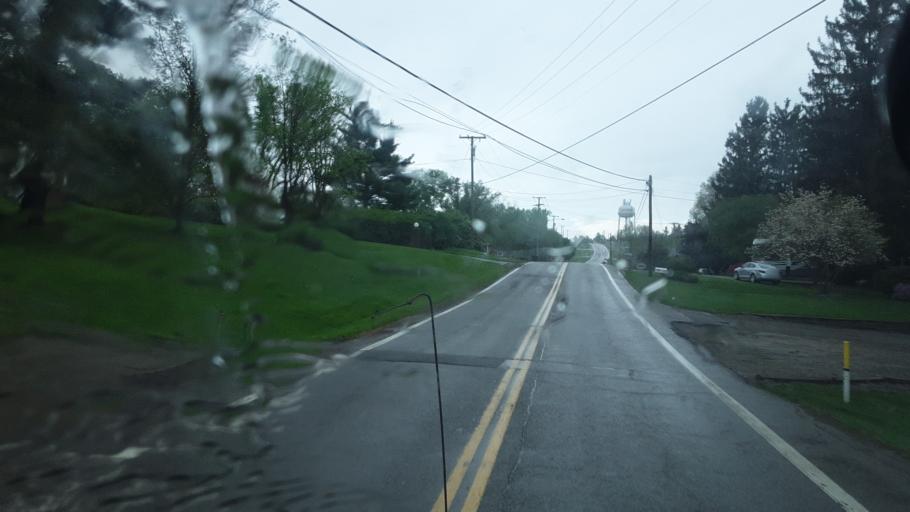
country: US
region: Ohio
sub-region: Muskingum County
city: New Concord
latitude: 40.0019
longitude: -81.7443
